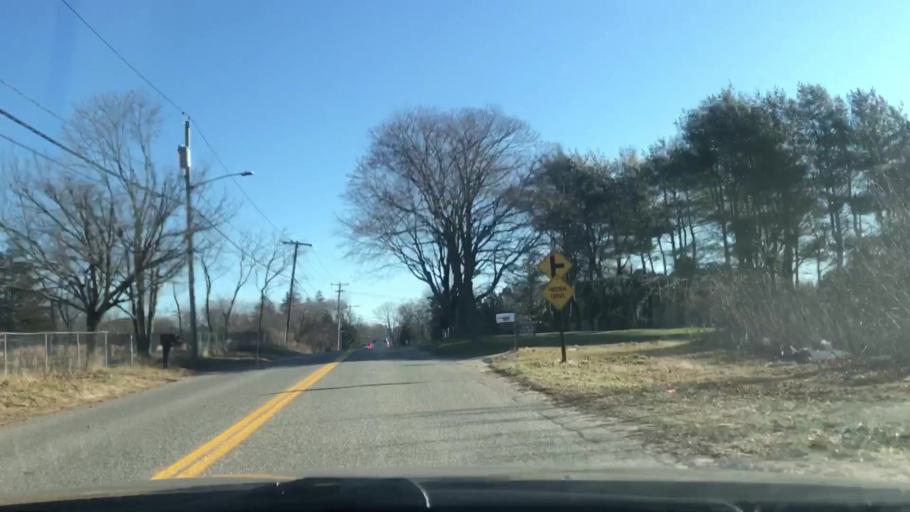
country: US
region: New York
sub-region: Suffolk County
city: Riverhead
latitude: 40.9361
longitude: -72.6877
